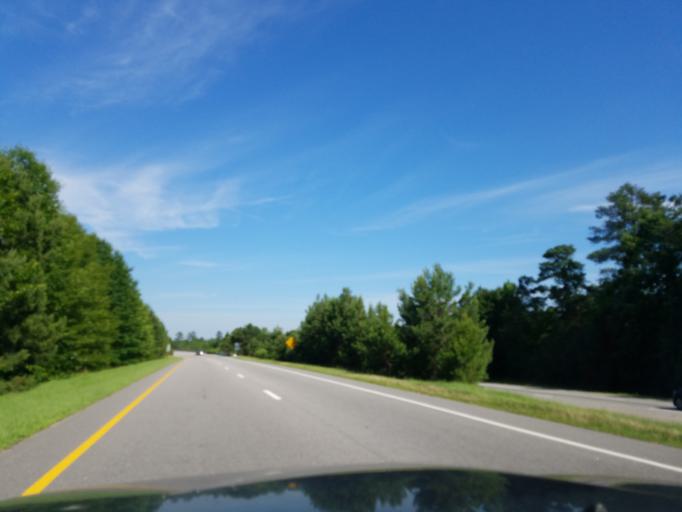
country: US
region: North Carolina
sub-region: Wake County
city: Raleigh
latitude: 35.8751
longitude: -78.5799
